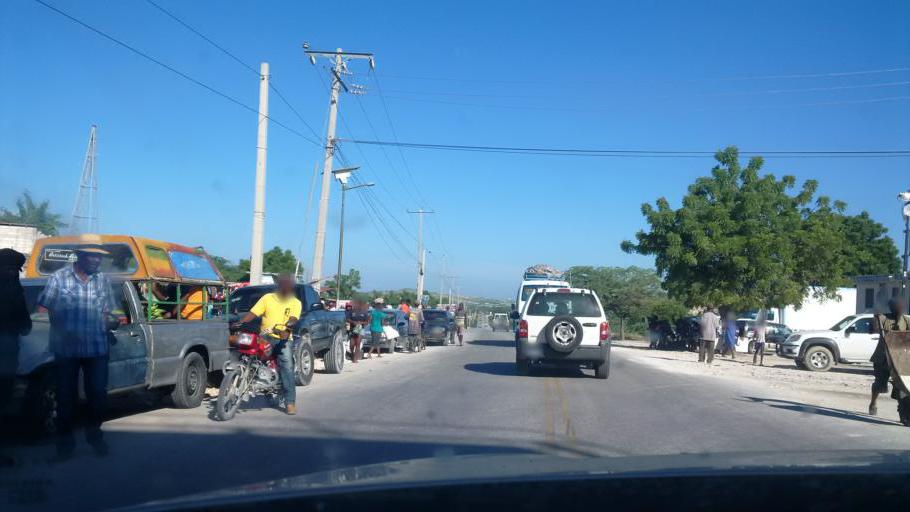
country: HT
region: Ouest
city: Cabaret
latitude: 18.7096
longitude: -72.3468
